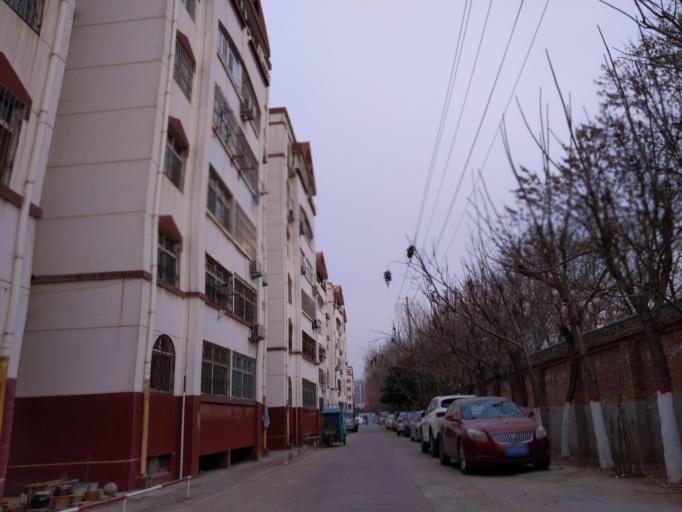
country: CN
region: Henan Sheng
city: Zhongyuanlu
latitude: 35.7554
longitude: 115.0515
